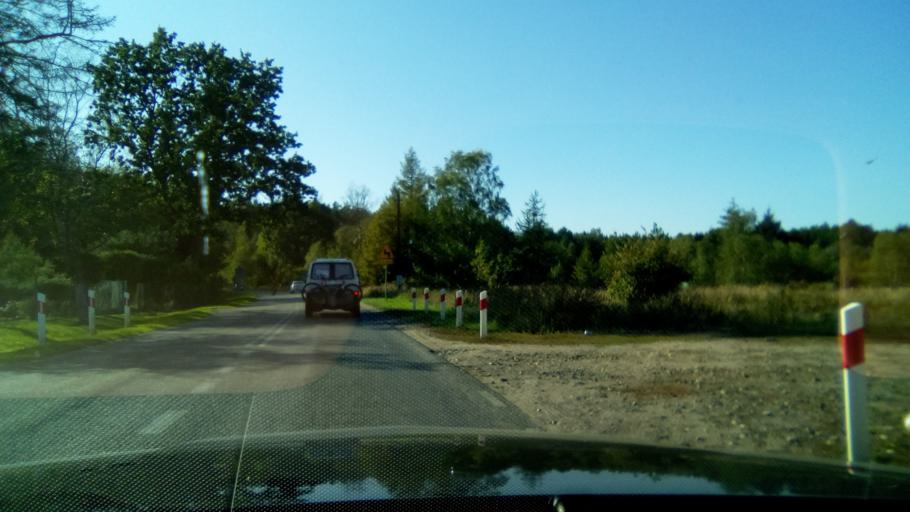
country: PL
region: West Pomeranian Voivodeship
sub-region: Powiat goleniowski
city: Przybiernow
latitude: 53.8245
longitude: 14.8320
